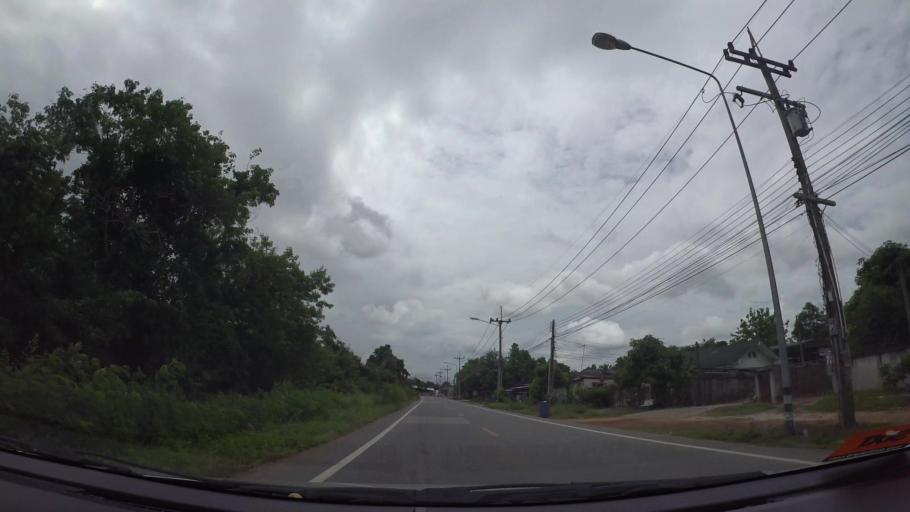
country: TH
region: Chon Buri
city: Si Racha
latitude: 13.1833
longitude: 100.9662
